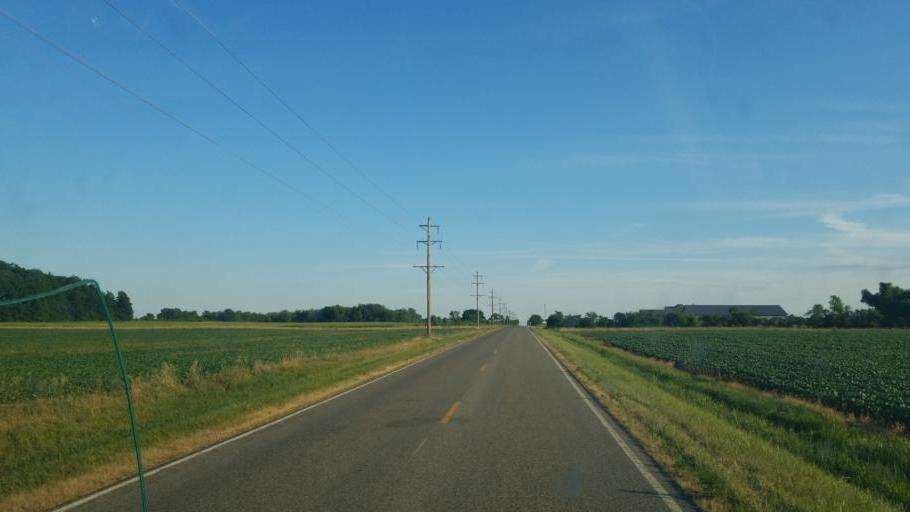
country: US
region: Ohio
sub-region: Williams County
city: Edgerton
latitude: 41.3769
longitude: -84.7671
